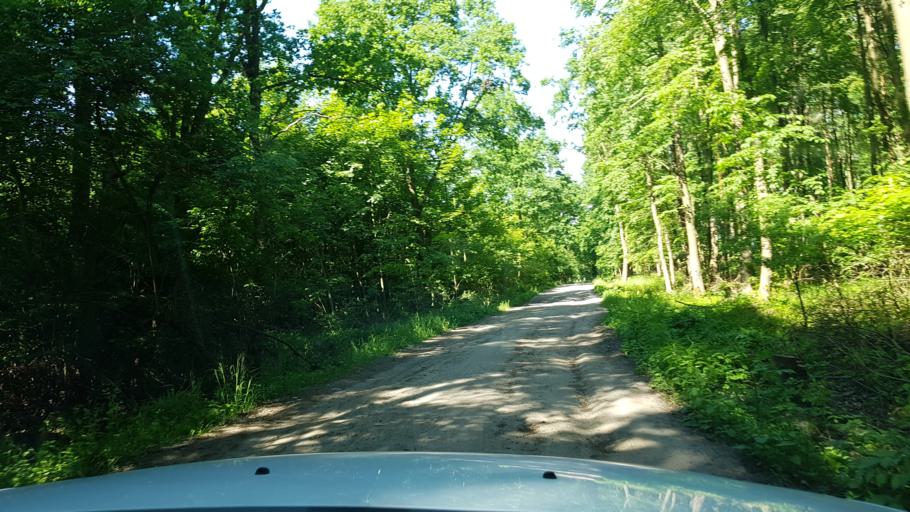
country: PL
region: West Pomeranian Voivodeship
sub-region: Powiat gryfinski
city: Banie
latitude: 53.1207
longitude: 14.5424
